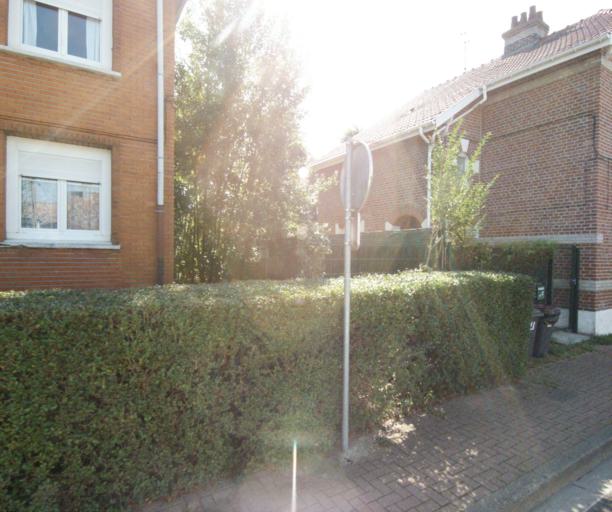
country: FR
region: Nord-Pas-de-Calais
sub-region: Departement du Nord
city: Mons-en-Baroeul
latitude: 50.6318
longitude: 3.1076
